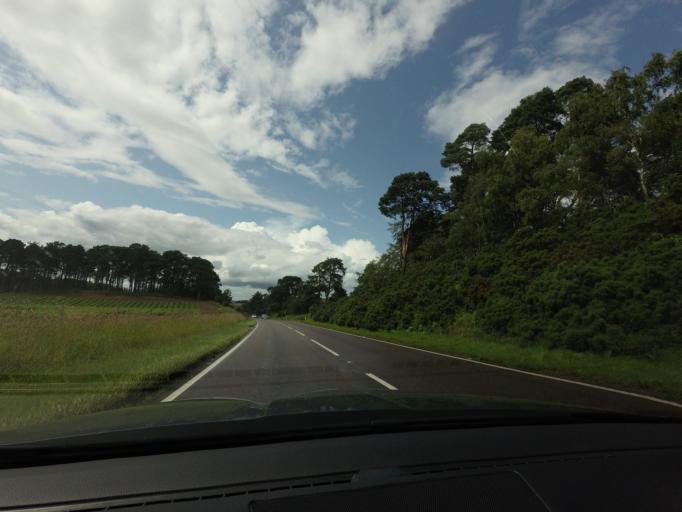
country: GB
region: Scotland
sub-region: Moray
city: Lhanbryd
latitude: 57.6340
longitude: -3.1893
